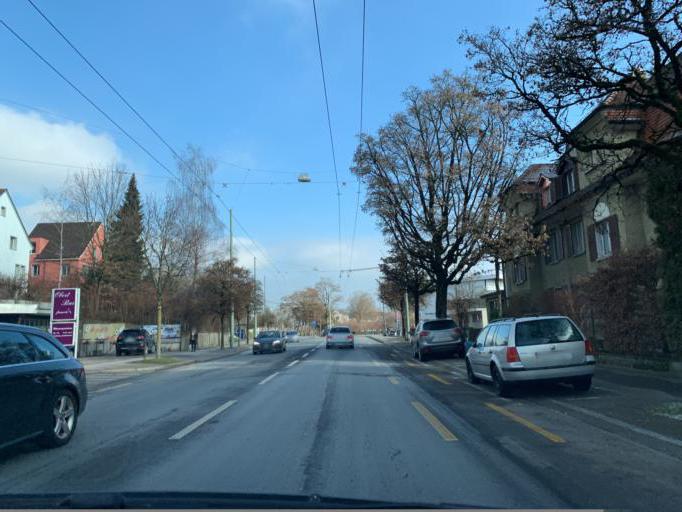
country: CH
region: Zurich
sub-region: Bezirk Winterthur
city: Oberwinterthur (Kreis 2) / Talacker
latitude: 47.5042
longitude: 8.7539
